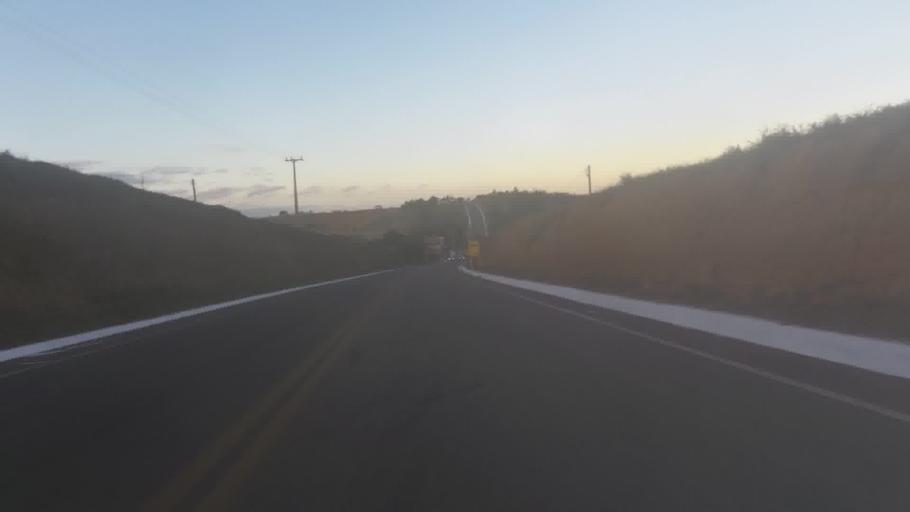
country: BR
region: Espirito Santo
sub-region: Marataizes
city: Marataizes
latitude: -21.1339
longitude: -40.8708
